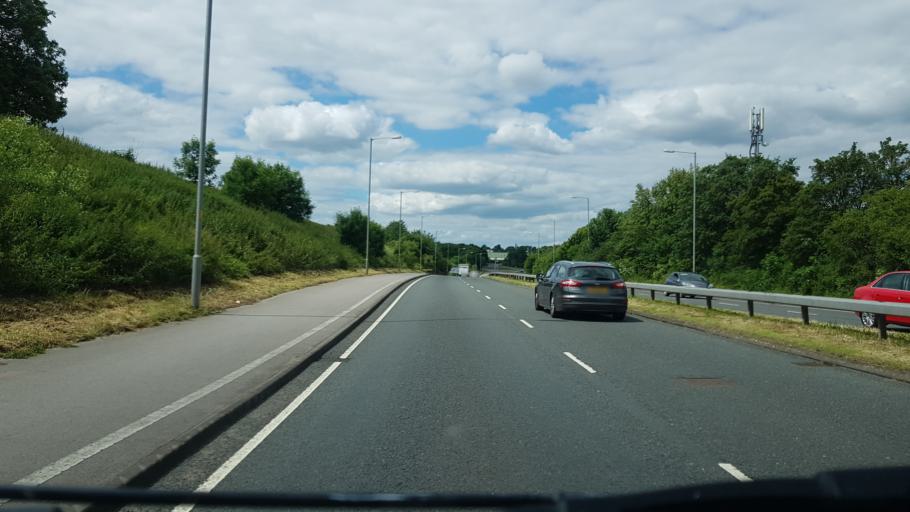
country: GB
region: England
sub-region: Worcestershire
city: Droitwich
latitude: 52.2789
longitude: -2.1624
